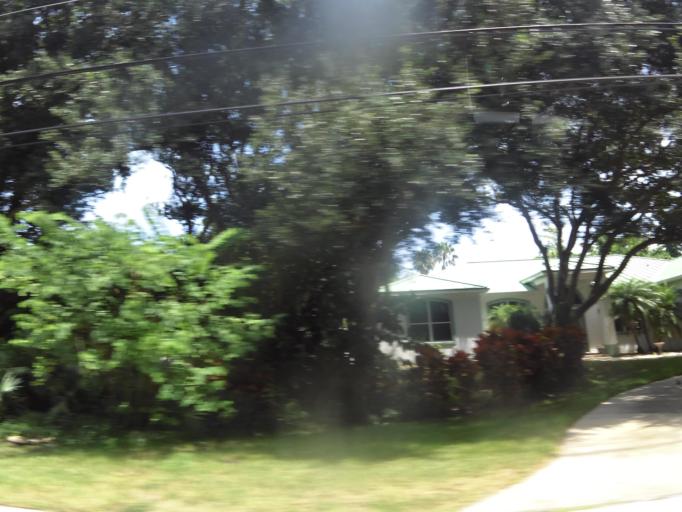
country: US
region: Florida
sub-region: Volusia County
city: Ponce Inlet
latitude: 29.1071
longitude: -80.9455
